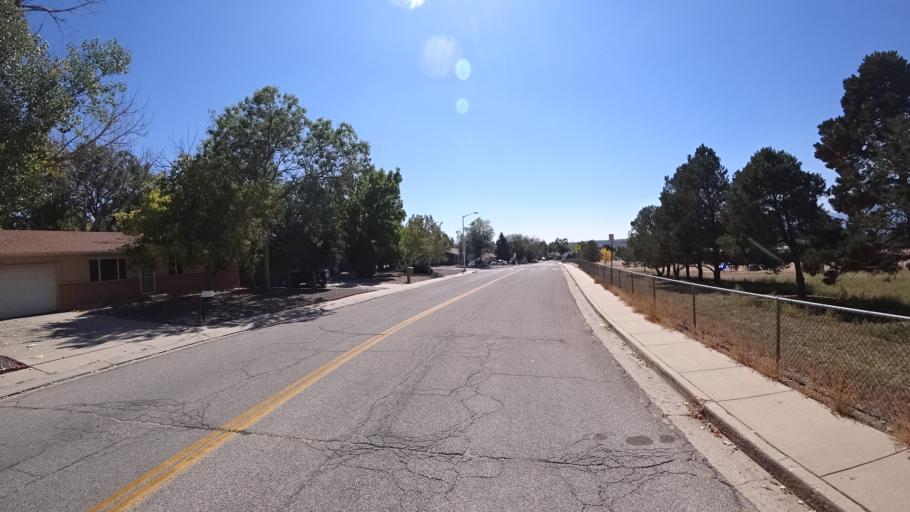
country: US
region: Colorado
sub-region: El Paso County
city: Cimarron Hills
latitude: 38.9086
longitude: -104.7702
